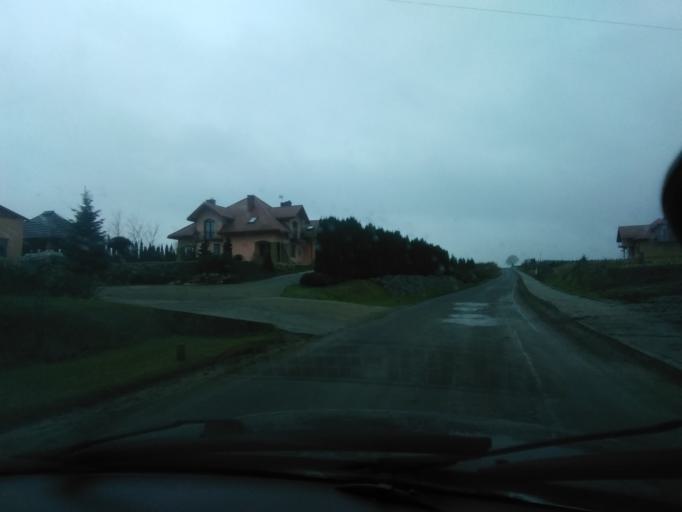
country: PL
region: Subcarpathian Voivodeship
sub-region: Powiat jaroslawski
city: Rokietnica
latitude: 49.9150
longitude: 22.6129
